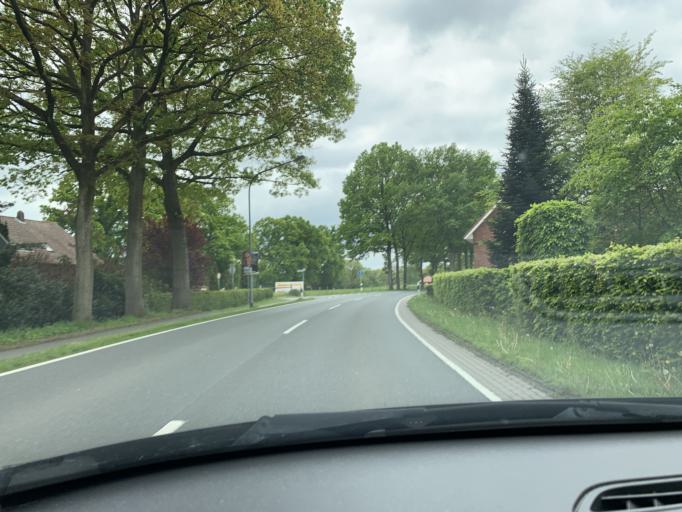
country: DE
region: Lower Saxony
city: Westerstede
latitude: 53.2464
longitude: 7.9252
